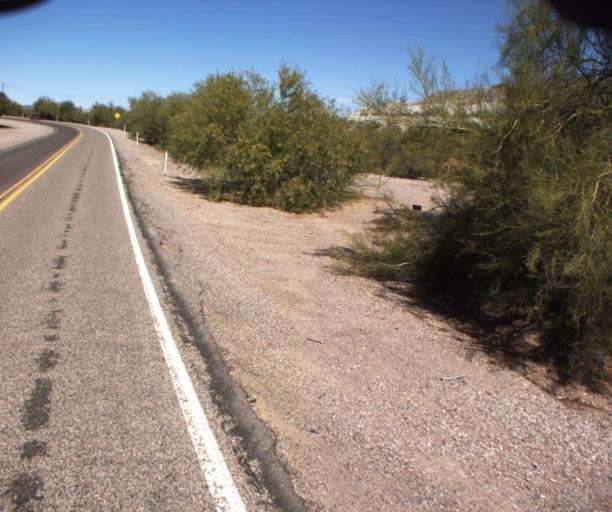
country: US
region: Arizona
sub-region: Pima County
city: Ajo
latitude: 32.3703
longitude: -112.8540
